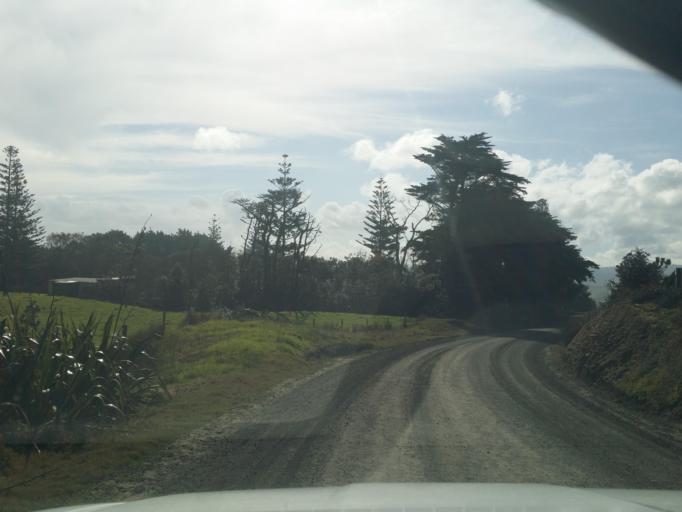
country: NZ
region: Northland
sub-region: Kaipara District
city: Dargaville
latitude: -35.8448
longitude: 173.6605
